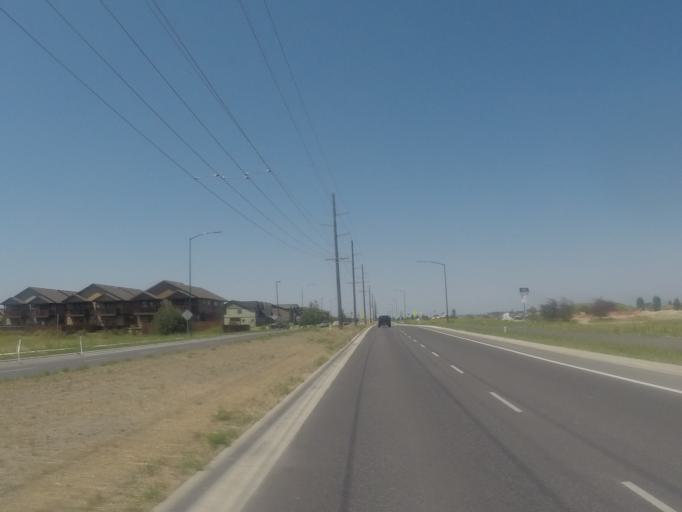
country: US
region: Montana
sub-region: Gallatin County
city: Bozeman
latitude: 45.6930
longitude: -111.0844
